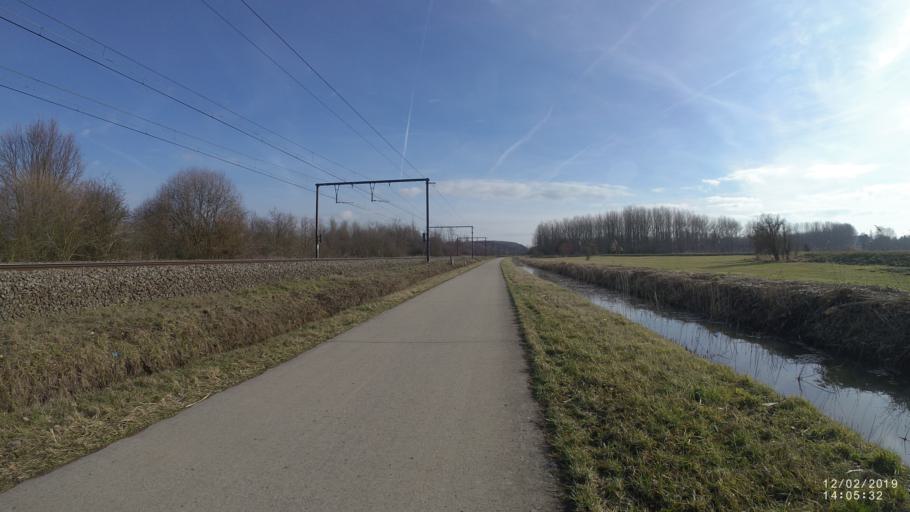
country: BE
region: Flanders
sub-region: Provincie Vlaams-Brabant
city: Scherpenheuvel-Zichem
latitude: 51.0018
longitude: 5.0002
